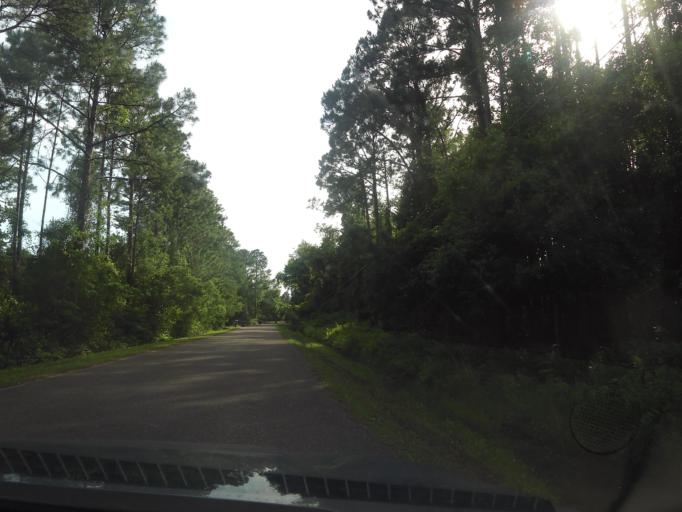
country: US
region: Florida
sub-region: Nassau County
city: Fernandina Beach
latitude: 30.5259
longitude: -81.4882
